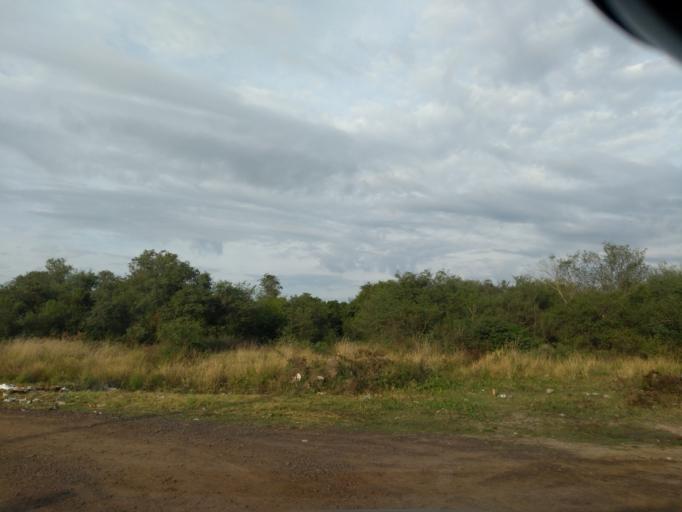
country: AR
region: Chaco
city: Fontana
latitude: -27.4239
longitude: -59.0504
